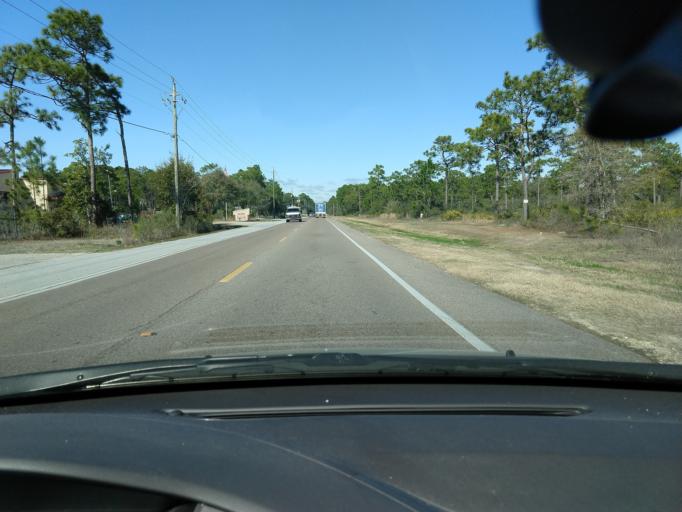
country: US
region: Florida
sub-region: Walton County
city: Miramar Beach
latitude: 30.3826
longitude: -86.3046
